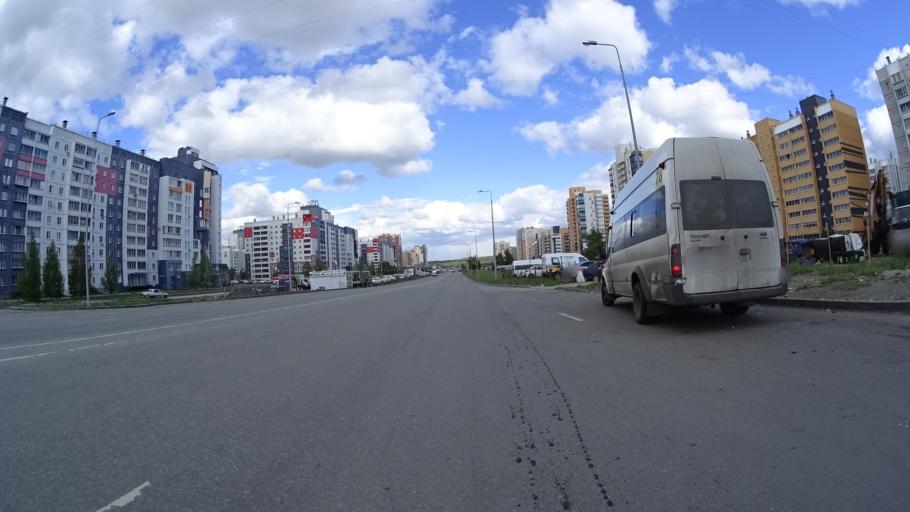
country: RU
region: Chelyabinsk
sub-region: Gorod Chelyabinsk
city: Chelyabinsk
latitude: 55.1636
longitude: 61.2859
